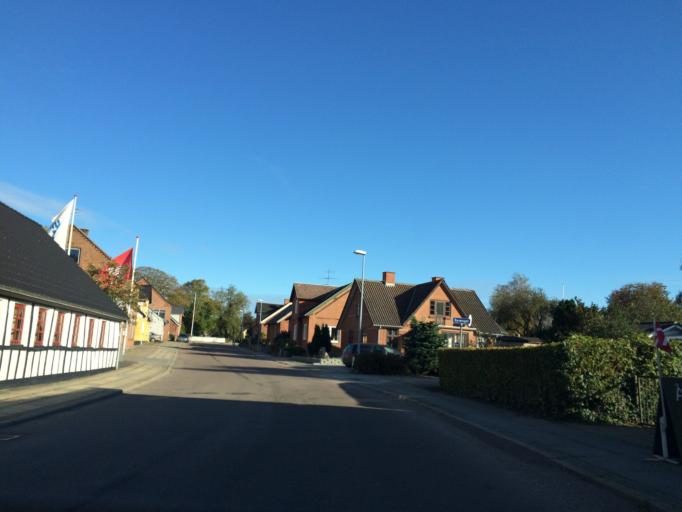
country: DK
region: Central Jutland
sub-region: Favrskov Kommune
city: Ulstrup
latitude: 56.3150
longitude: 9.7880
